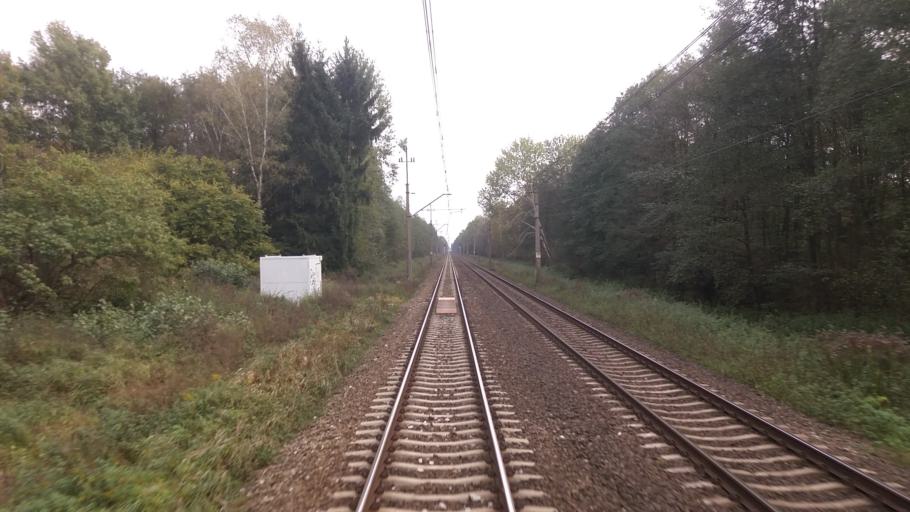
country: PL
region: West Pomeranian Voivodeship
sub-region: Powiat stargardzki
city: Kobylanka
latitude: 53.3778
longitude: 14.8158
